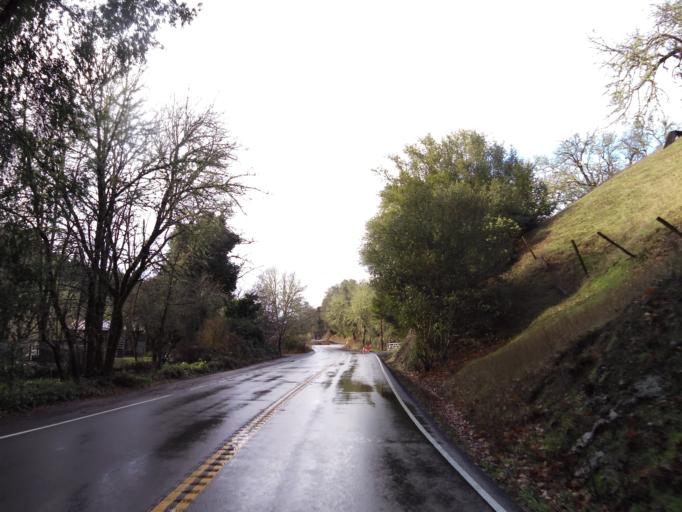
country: US
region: California
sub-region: Sonoma County
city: Cloverdale
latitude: 38.8856
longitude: -123.1604
